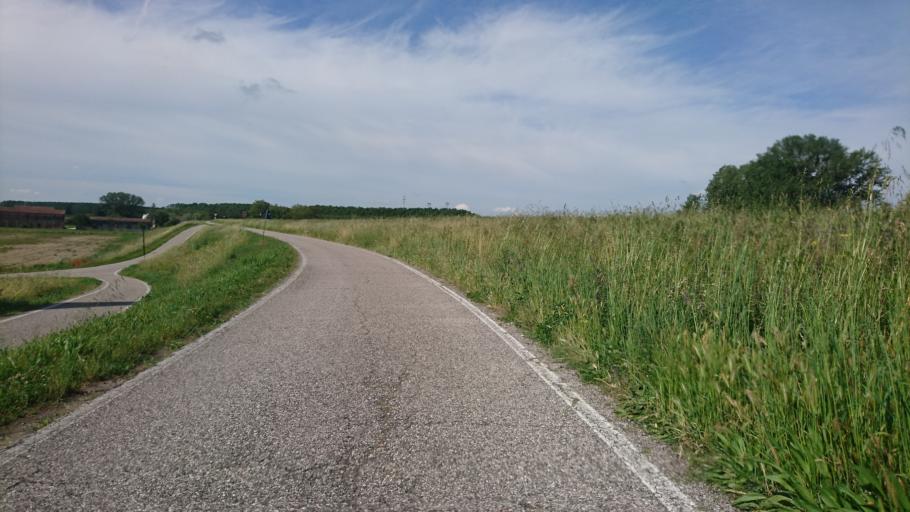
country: IT
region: Veneto
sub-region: Provincia di Rovigo
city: Melara
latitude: 45.0475
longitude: 11.1779
